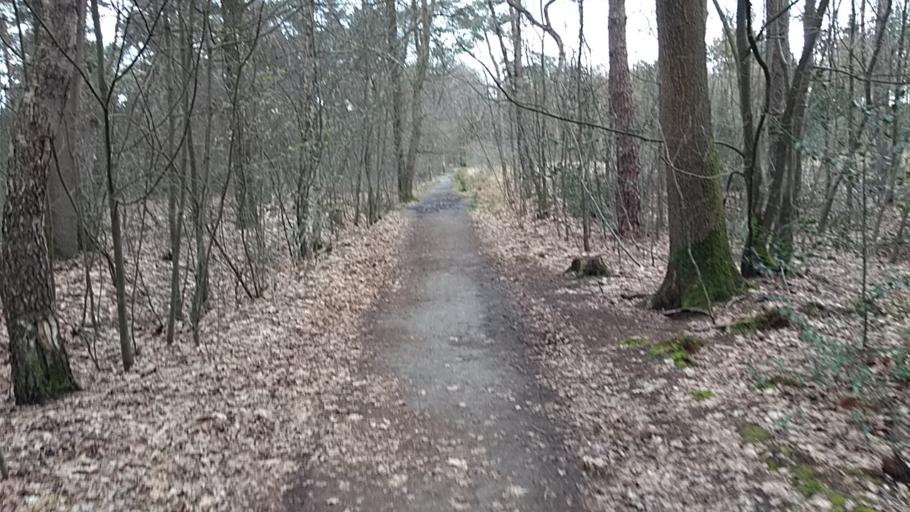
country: NL
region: Overijssel
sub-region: Gemeente Almelo
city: Almelo
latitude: 52.3328
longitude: 6.6697
